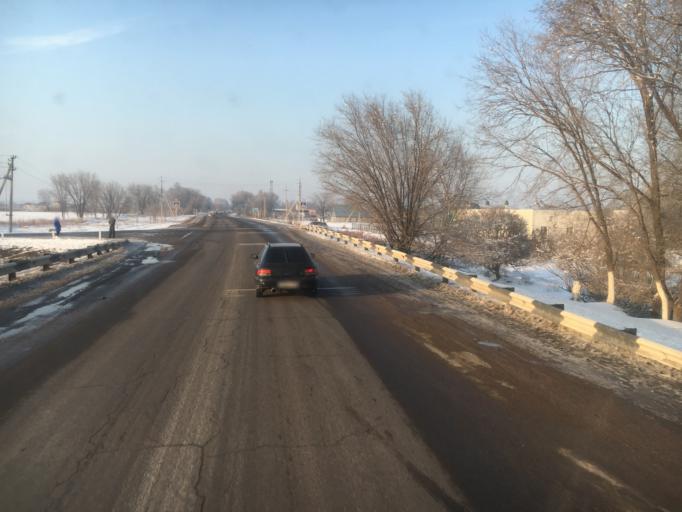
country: KZ
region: Almaty Oblysy
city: Burunday
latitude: 43.3320
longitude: 76.6618
